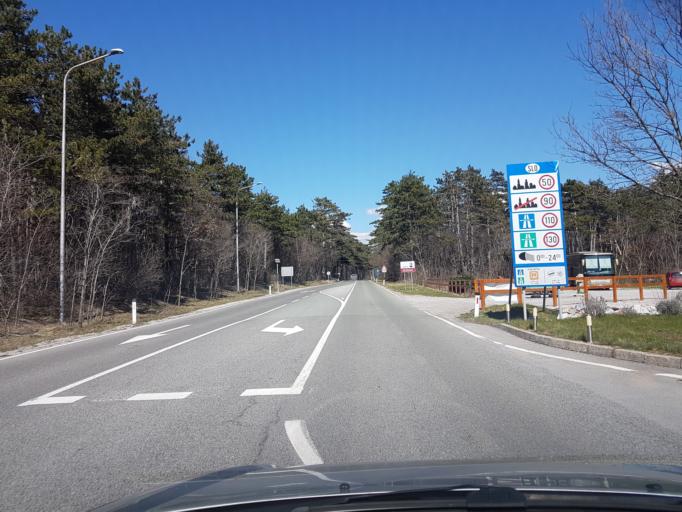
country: SI
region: Sezana
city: Sezana
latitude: 45.6536
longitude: 13.8805
